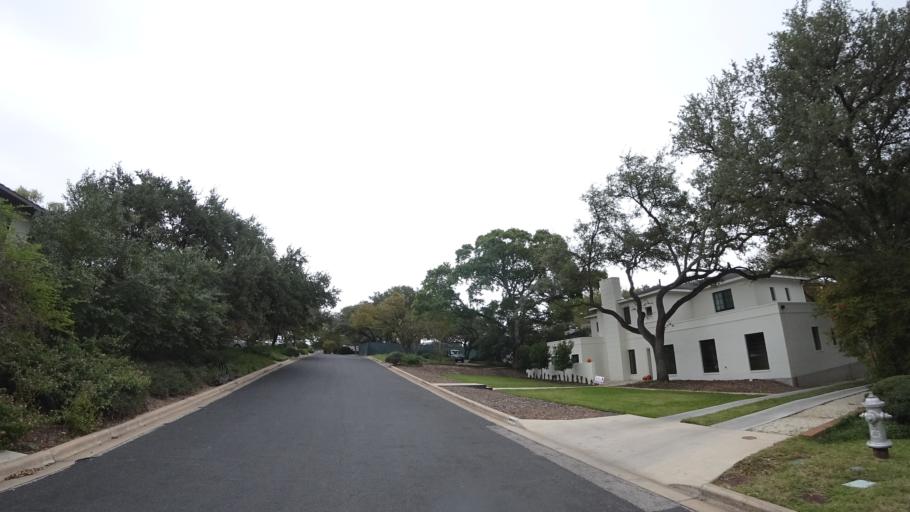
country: US
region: Texas
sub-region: Travis County
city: West Lake Hills
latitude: 30.3073
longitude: -97.7719
